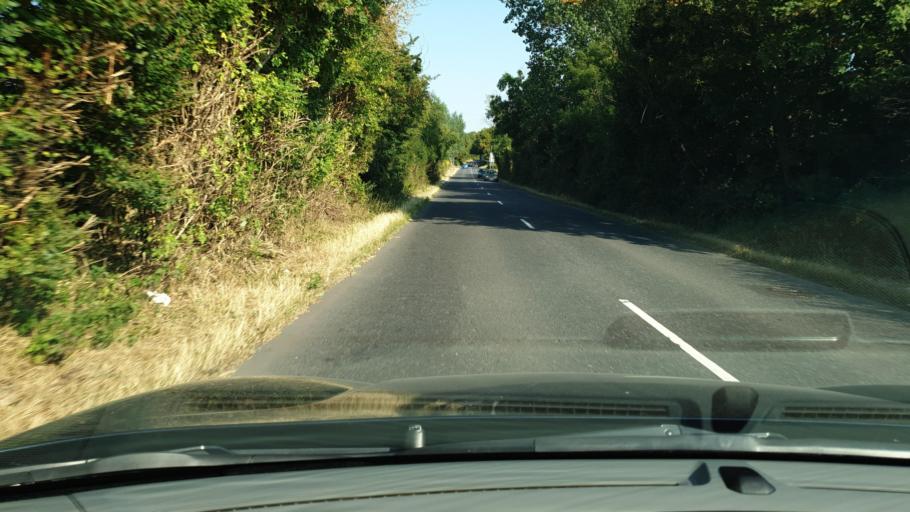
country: IE
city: Kentstown
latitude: 53.6264
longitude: -6.5282
